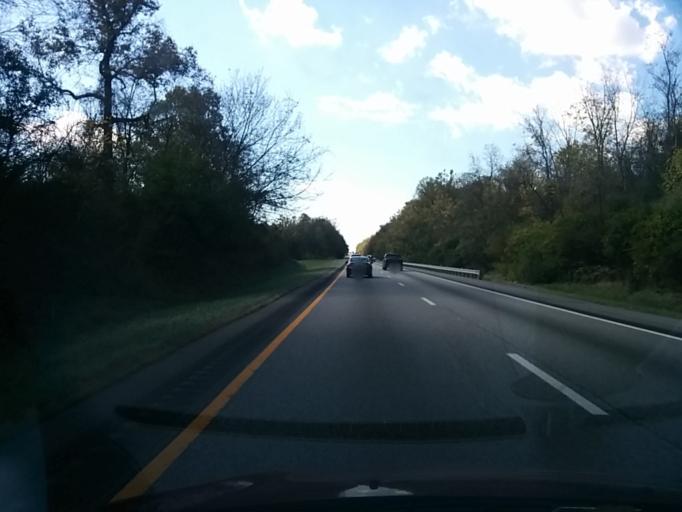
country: US
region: Virginia
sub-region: Botetourt County
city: Daleville
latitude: 37.4331
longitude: -79.8731
